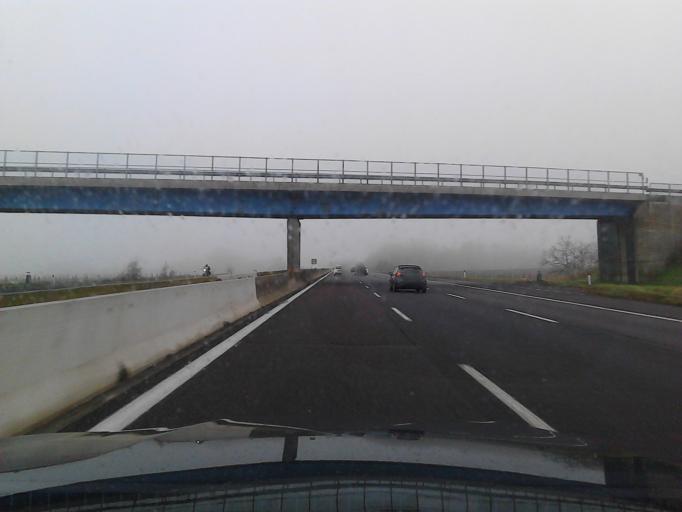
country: IT
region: Emilia-Romagna
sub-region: Provincia di Bologna
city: Imola
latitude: 44.3962
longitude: 11.7019
